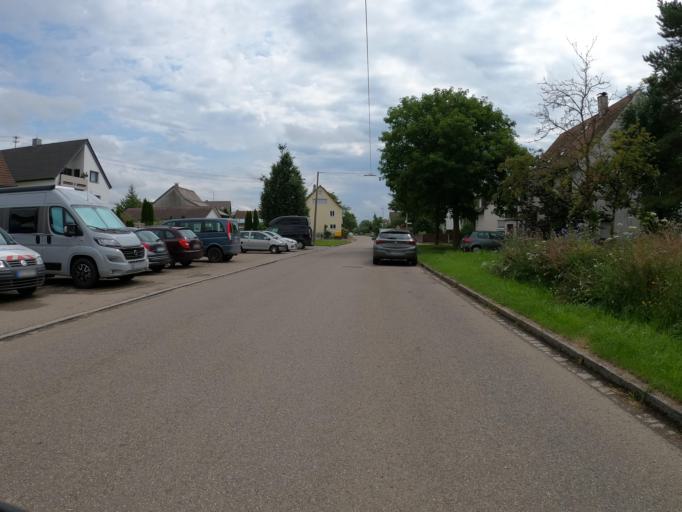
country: DE
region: Baden-Wuerttemberg
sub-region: Tuebingen Region
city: Langenau
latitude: 48.5041
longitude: 10.1375
